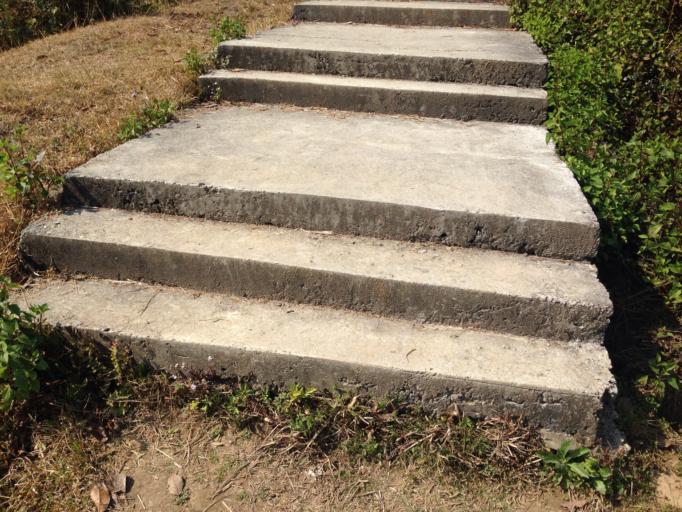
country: NP
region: Western Region
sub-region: Gandaki Zone
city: Pokhara
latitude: 28.2012
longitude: 83.9437
